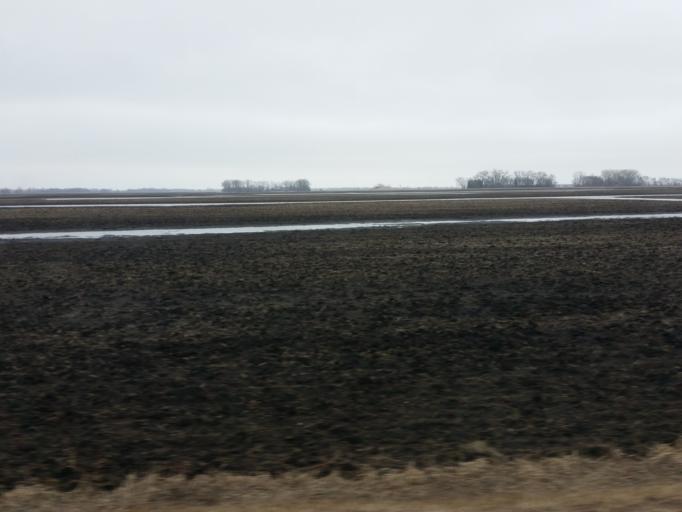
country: US
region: North Dakota
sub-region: Walsh County
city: Grafton
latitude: 48.3857
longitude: -97.2119
